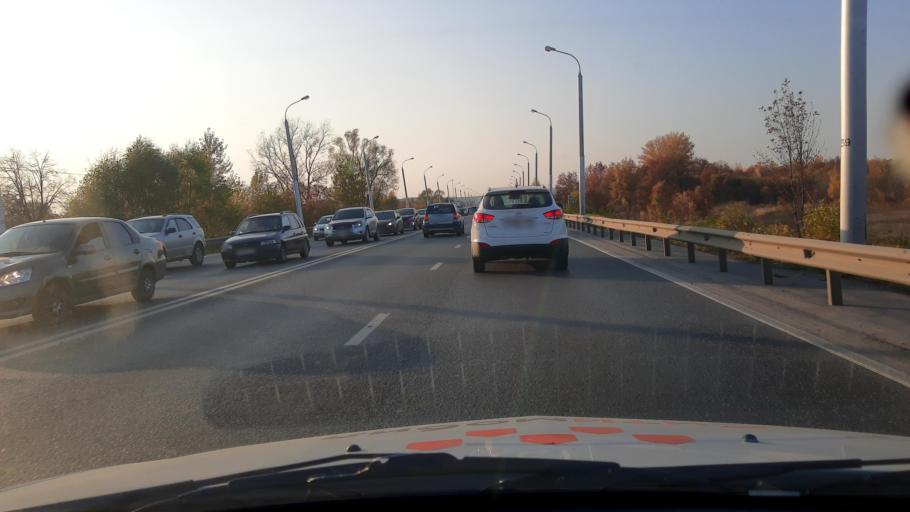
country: RU
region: Bashkortostan
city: Iglino
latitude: 54.8006
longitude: 56.1974
